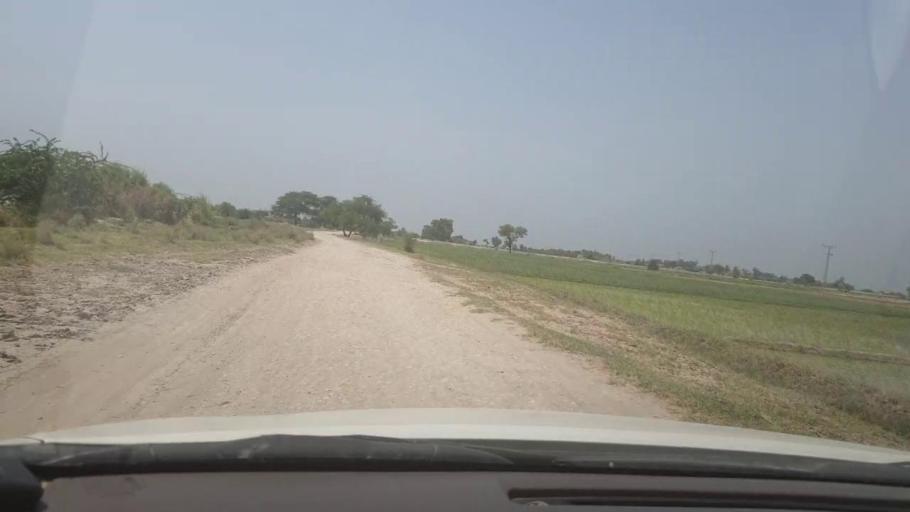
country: PK
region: Sindh
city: Shikarpur
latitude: 27.9397
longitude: 68.5744
